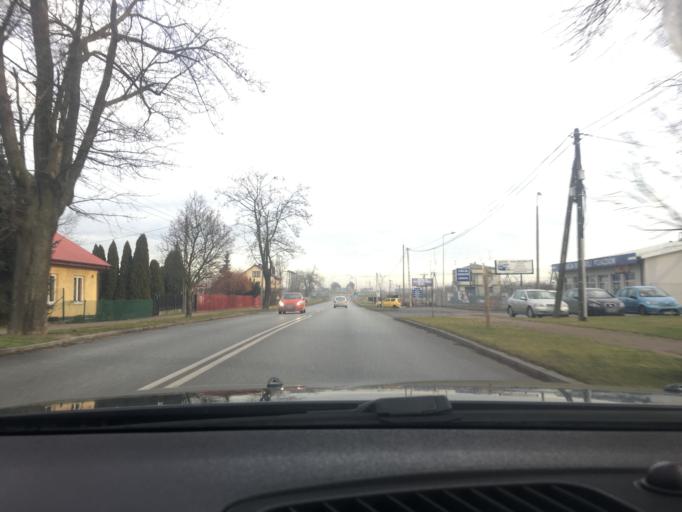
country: PL
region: Swietokrzyskie
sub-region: Powiat jedrzejowski
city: Jedrzejow
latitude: 50.6442
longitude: 20.3112
